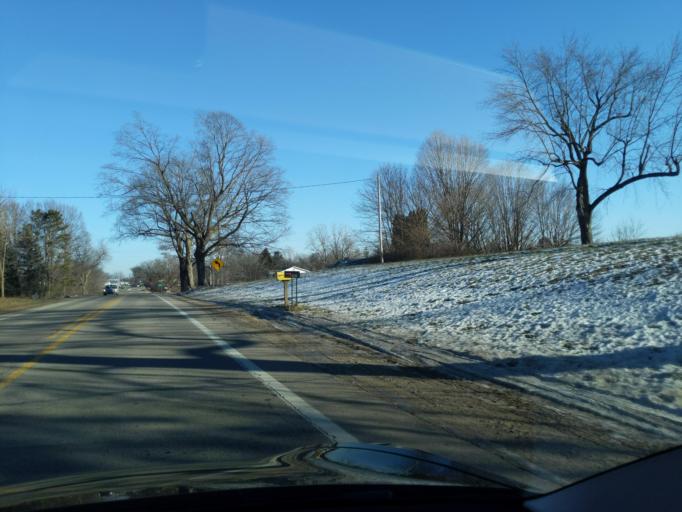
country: US
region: Michigan
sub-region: Ingham County
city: Stockbridge
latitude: 42.3937
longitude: -84.2569
